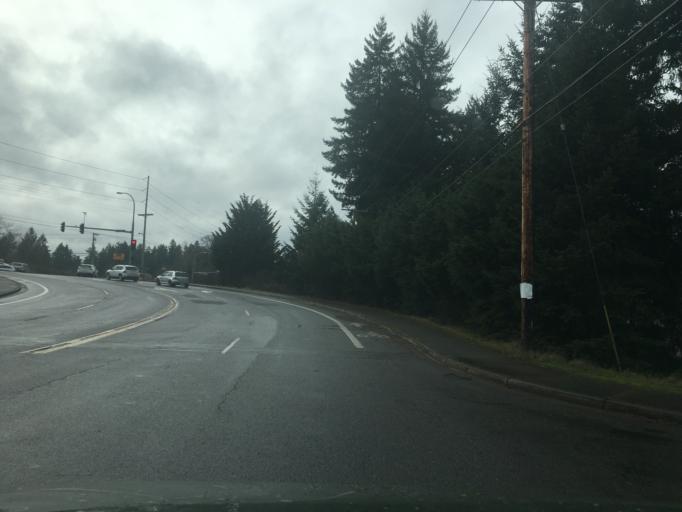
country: US
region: Washington
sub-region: Thurston County
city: Tanglewilde-Thompson Place
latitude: 47.0429
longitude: -122.7807
